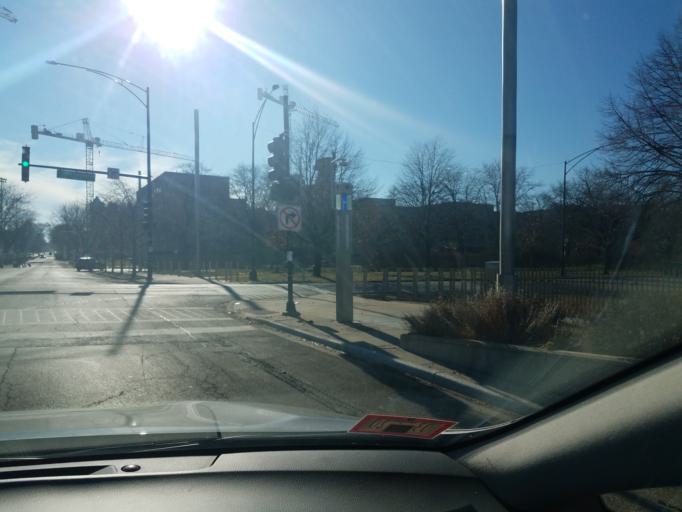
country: US
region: Illinois
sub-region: Cook County
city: Chicago
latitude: 41.7867
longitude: -87.5964
